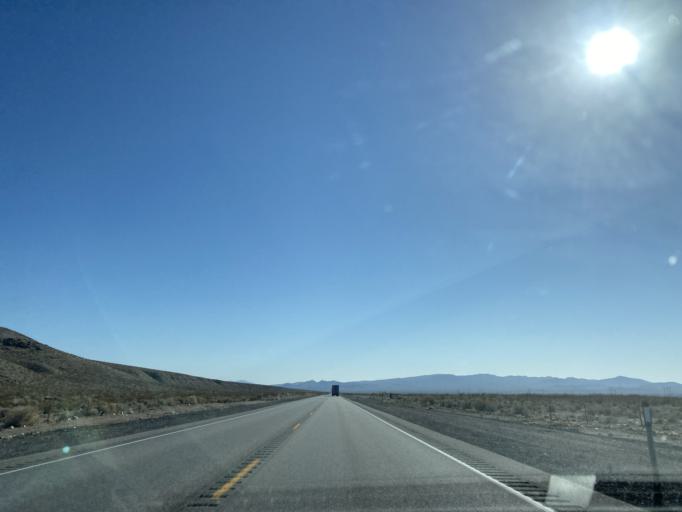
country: US
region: Nevada
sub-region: Nye County
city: Beatty
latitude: 36.8763
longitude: -116.7539
